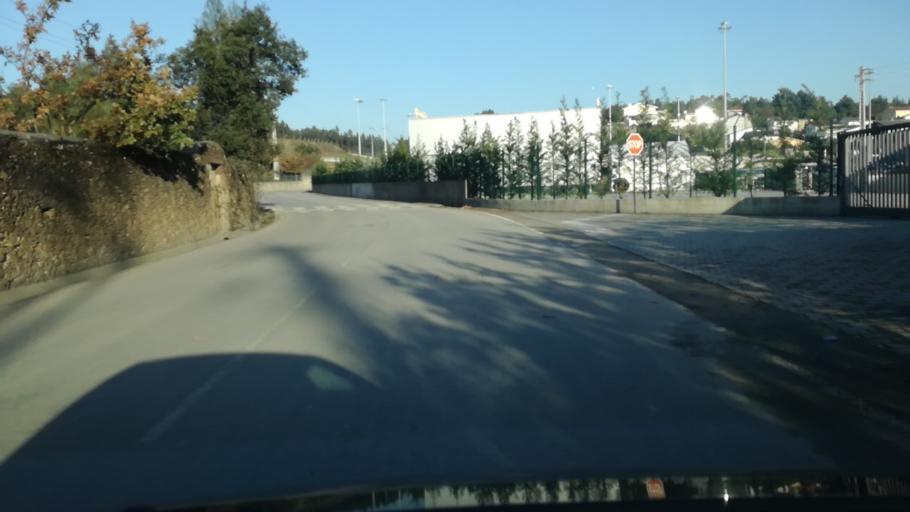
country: PT
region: Braga
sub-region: Vila Nova de Famalicao
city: Ferreiros
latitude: 41.3576
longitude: -8.5421
